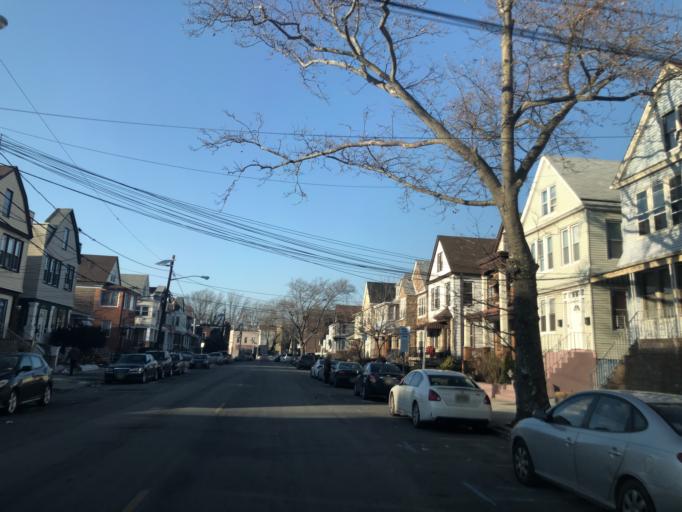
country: US
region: New Jersey
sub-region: Hudson County
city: Jersey City
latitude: 40.6979
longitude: -74.0839
